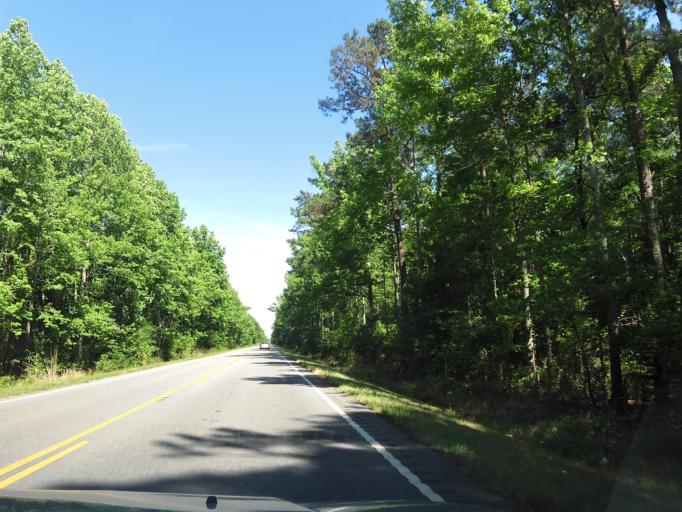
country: US
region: South Carolina
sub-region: Barnwell County
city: Blackville
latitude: 33.3653
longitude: -81.3245
